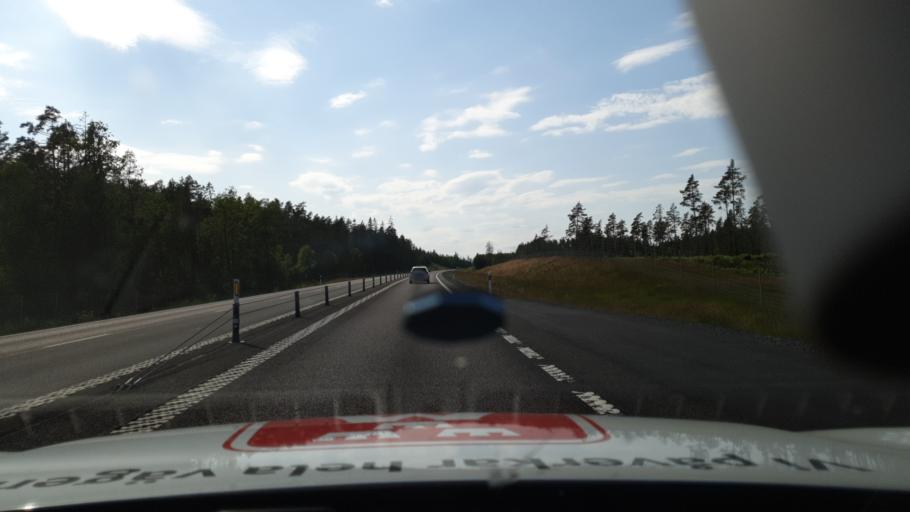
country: SE
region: Joenkoeping
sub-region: Mullsjo Kommun
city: Mullsjoe
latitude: 57.8665
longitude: 13.9700
